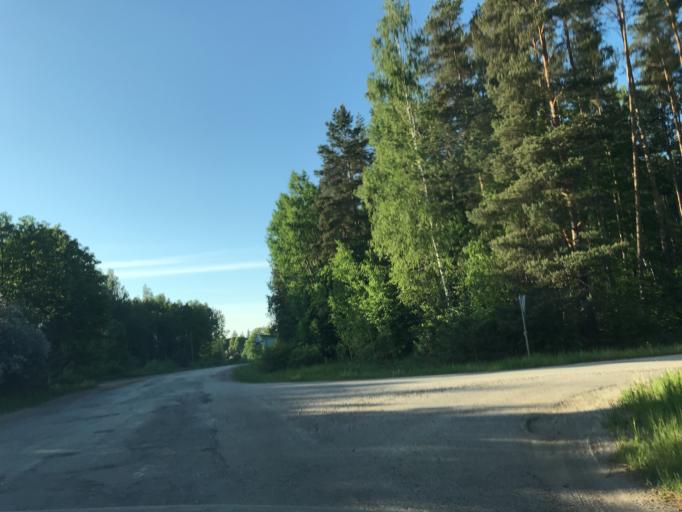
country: LV
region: Ozolnieku
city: Ozolnieki
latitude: 56.6051
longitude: 23.7912
